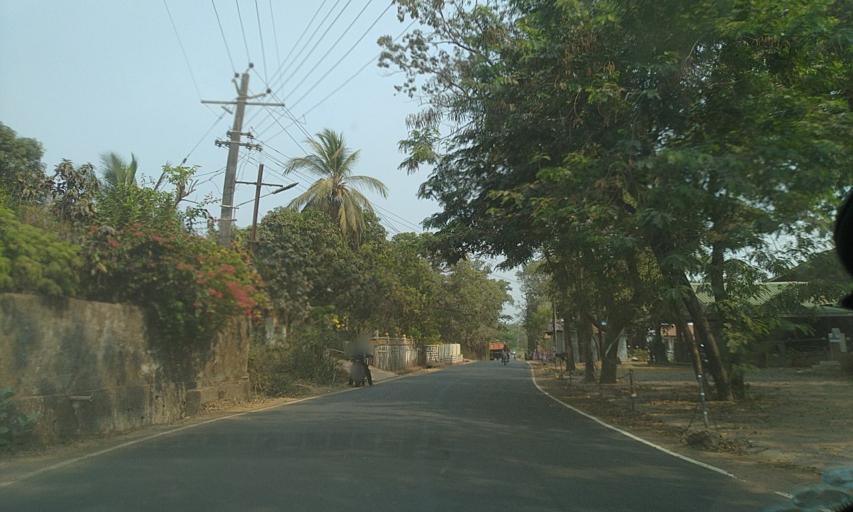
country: IN
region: Goa
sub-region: South Goa
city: Quepem
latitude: 15.2602
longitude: 74.0472
